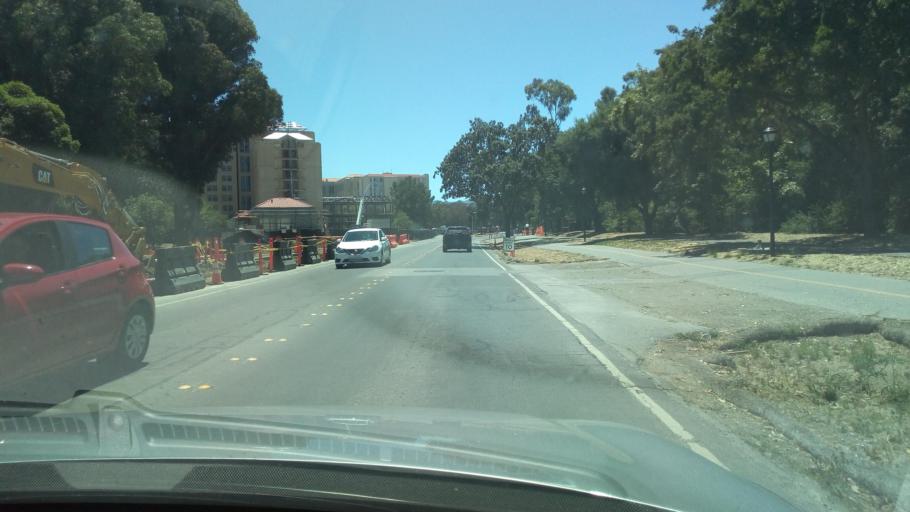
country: US
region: California
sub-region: Santa Clara County
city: Stanford
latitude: 37.4288
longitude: -122.1555
